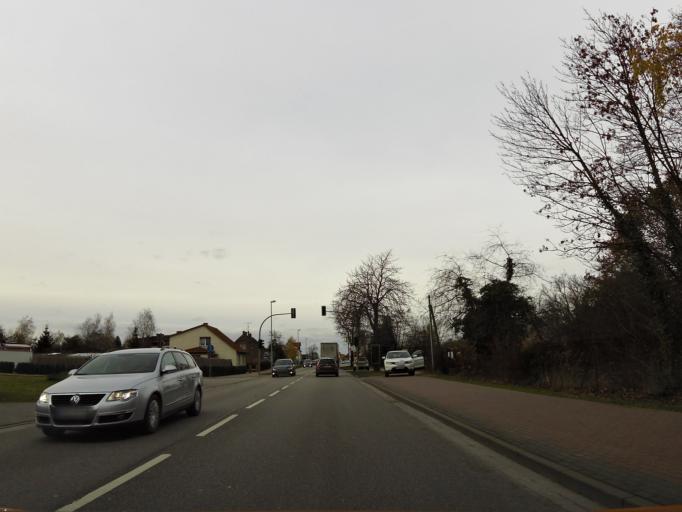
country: DE
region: Saxony-Anhalt
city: Salzwedel
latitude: 52.8395
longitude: 11.1740
